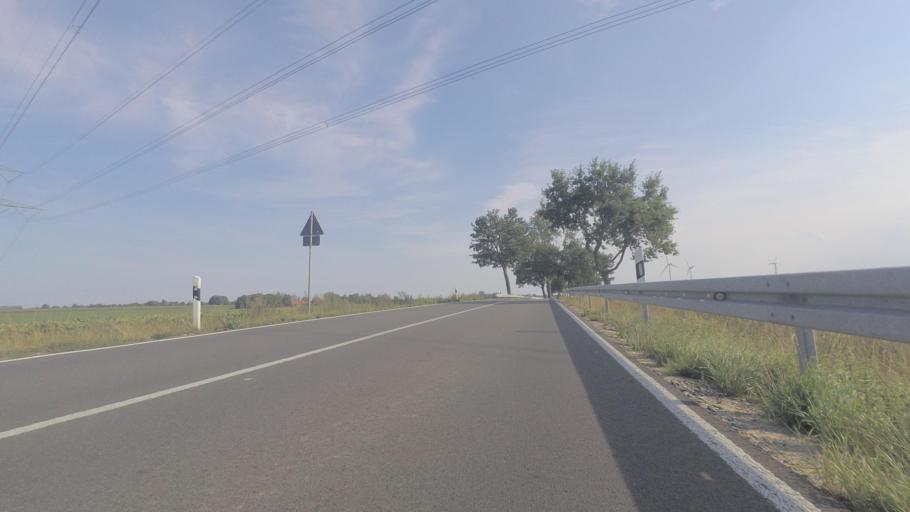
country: DE
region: Mecklenburg-Vorpommern
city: Grimmen
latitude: 54.0223
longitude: 13.1366
